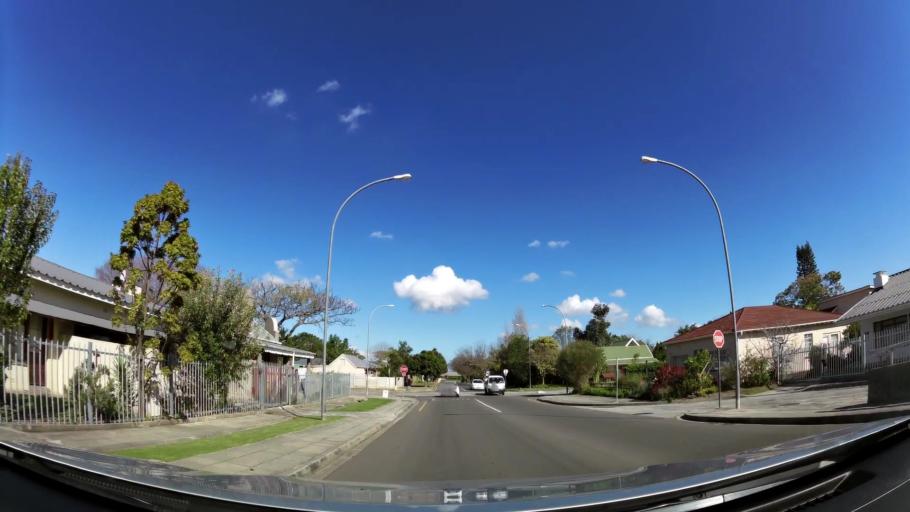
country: ZA
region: Western Cape
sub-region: Eden District Municipality
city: George
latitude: -33.9515
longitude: 22.4649
